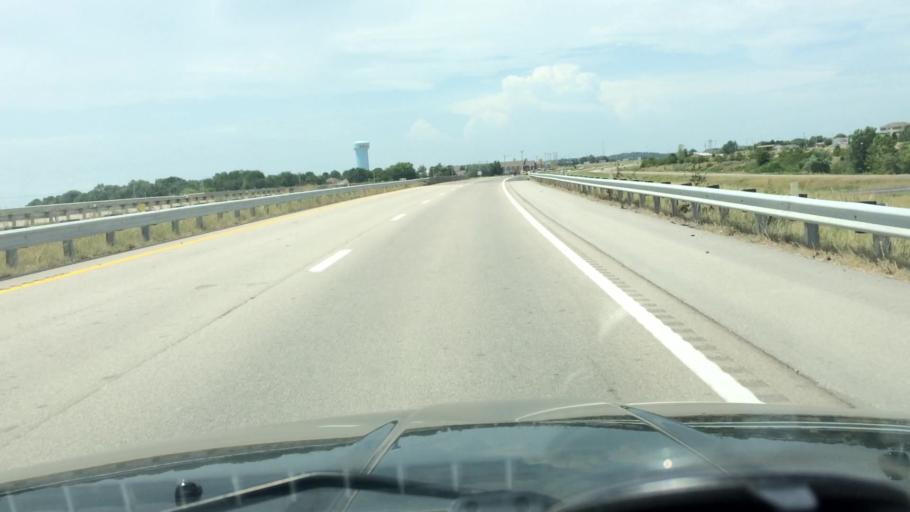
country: US
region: Missouri
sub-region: Polk County
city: Bolivar
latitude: 37.5922
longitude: -93.4311
